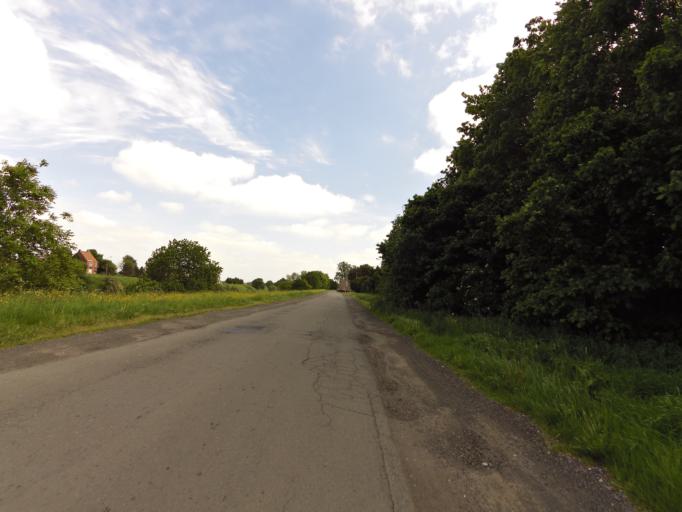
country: BE
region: Flanders
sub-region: Provincie Oost-Vlaanderen
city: Knesselare
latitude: 51.1144
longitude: 3.3961
